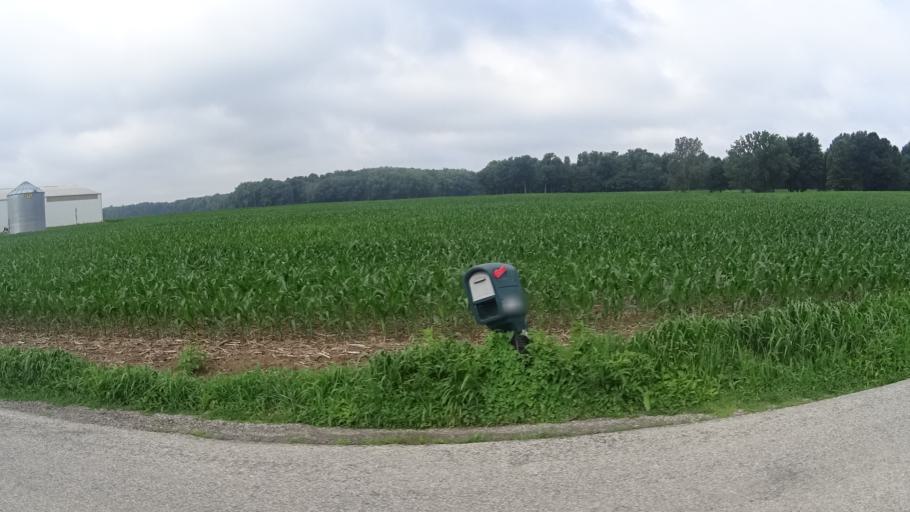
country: US
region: Ohio
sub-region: Erie County
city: Milan
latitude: 41.2979
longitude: -82.5123
